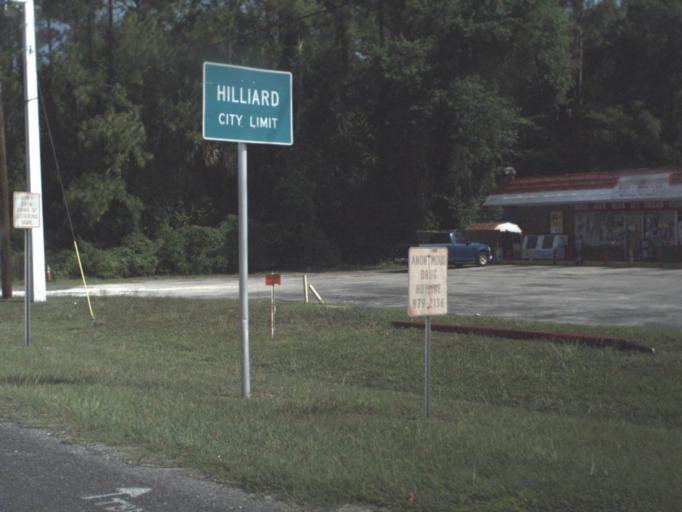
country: US
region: Florida
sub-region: Nassau County
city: Hilliard
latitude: 30.6764
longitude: -81.9050
